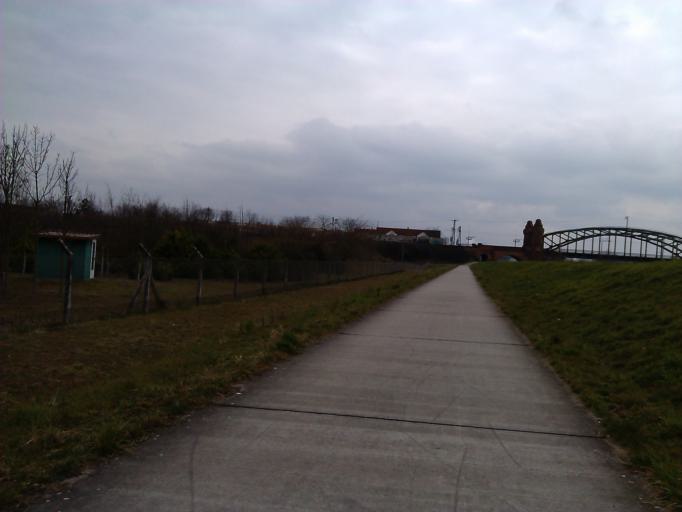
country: DE
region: Hesse
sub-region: Regierungsbezirk Darmstadt
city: Hochheim am Main
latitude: 49.9975
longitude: 8.3420
